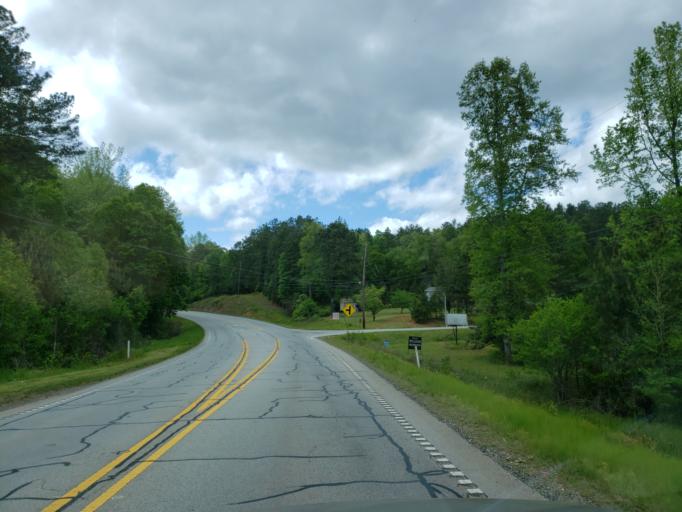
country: US
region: Georgia
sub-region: Haralson County
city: Tallapoosa
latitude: 33.7318
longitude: -85.2390
